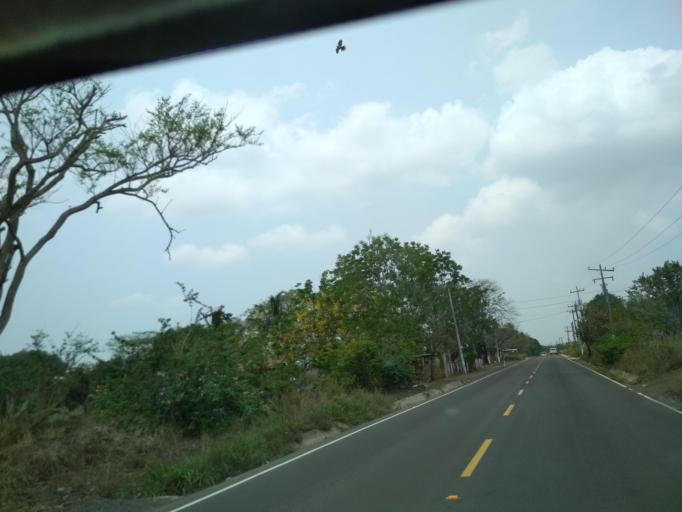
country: MX
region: Veracruz
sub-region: Veracruz
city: Delfino Victoria (Santa Fe)
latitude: 19.1540
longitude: -96.2931
